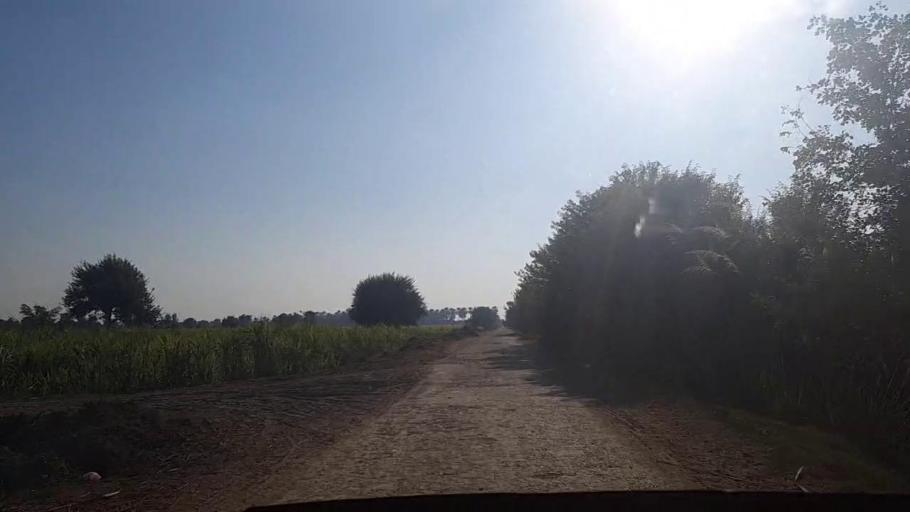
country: PK
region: Sindh
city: Gambat
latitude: 27.3591
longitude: 68.4565
